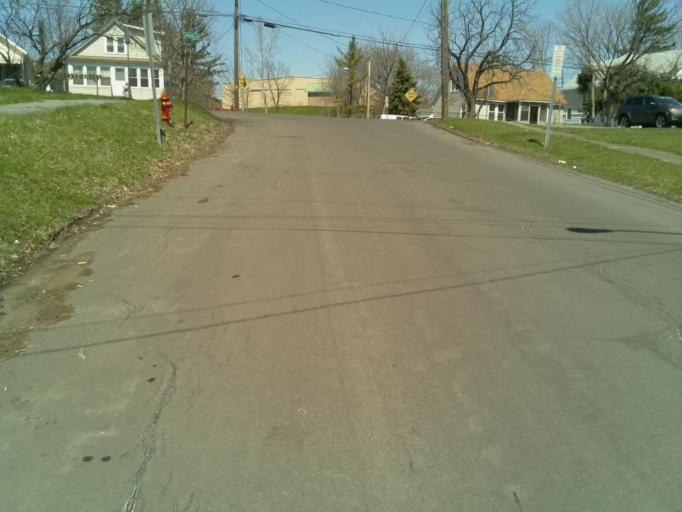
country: US
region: New York
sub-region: Onondaga County
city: Lyncourt
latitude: 43.0561
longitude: -76.1167
